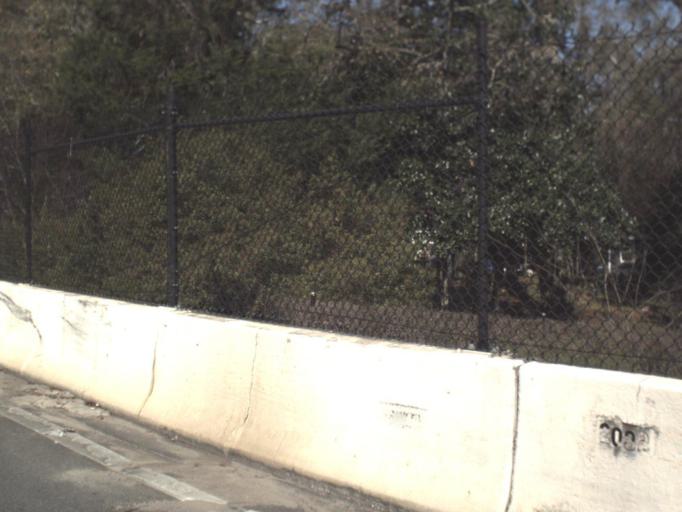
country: US
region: Florida
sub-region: Leon County
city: Tallahassee
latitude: 30.4402
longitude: -84.3069
